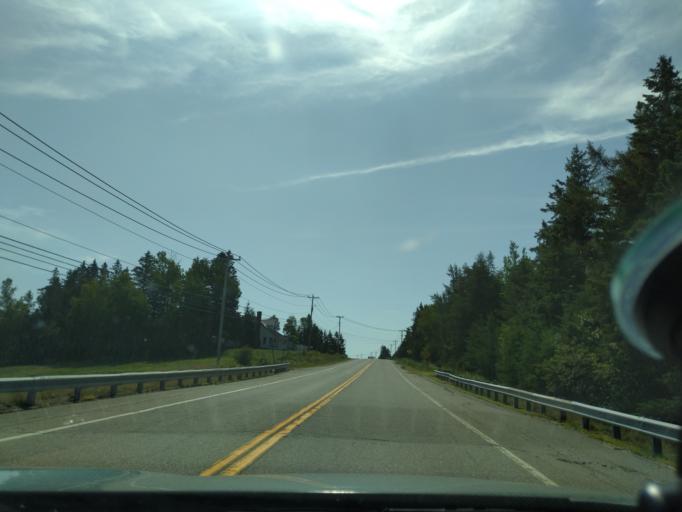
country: US
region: Maine
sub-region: Washington County
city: Addison
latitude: 44.6528
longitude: -67.7154
